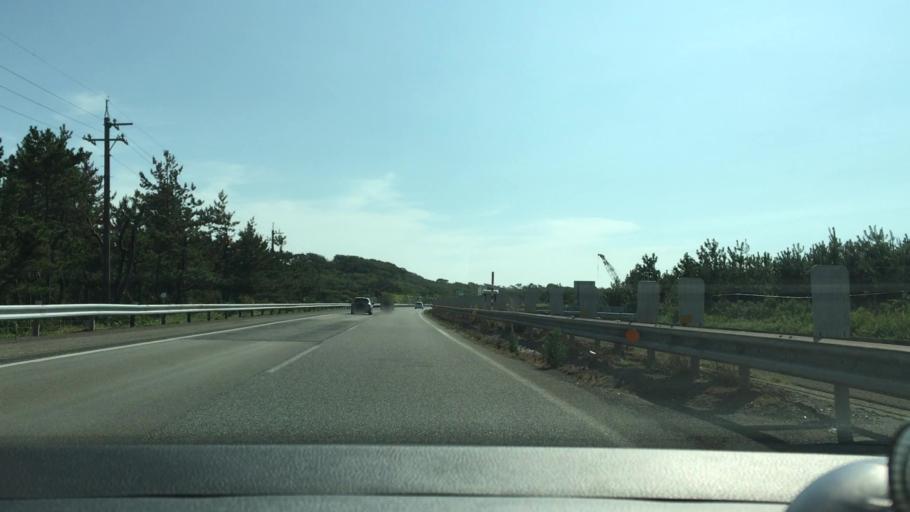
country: JP
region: Ishikawa
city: Komatsu
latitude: 36.3590
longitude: 136.3362
